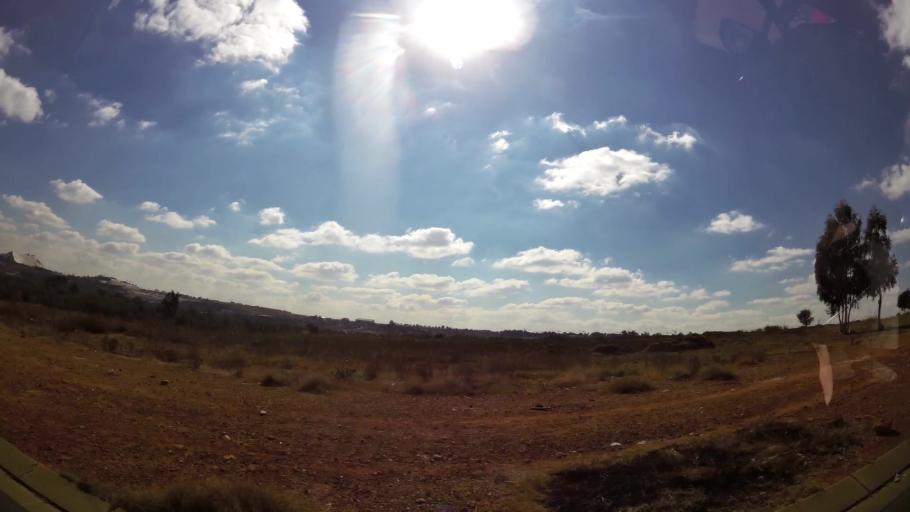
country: ZA
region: Gauteng
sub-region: West Rand District Municipality
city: Krugersdorp
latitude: -26.1375
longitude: 27.7891
